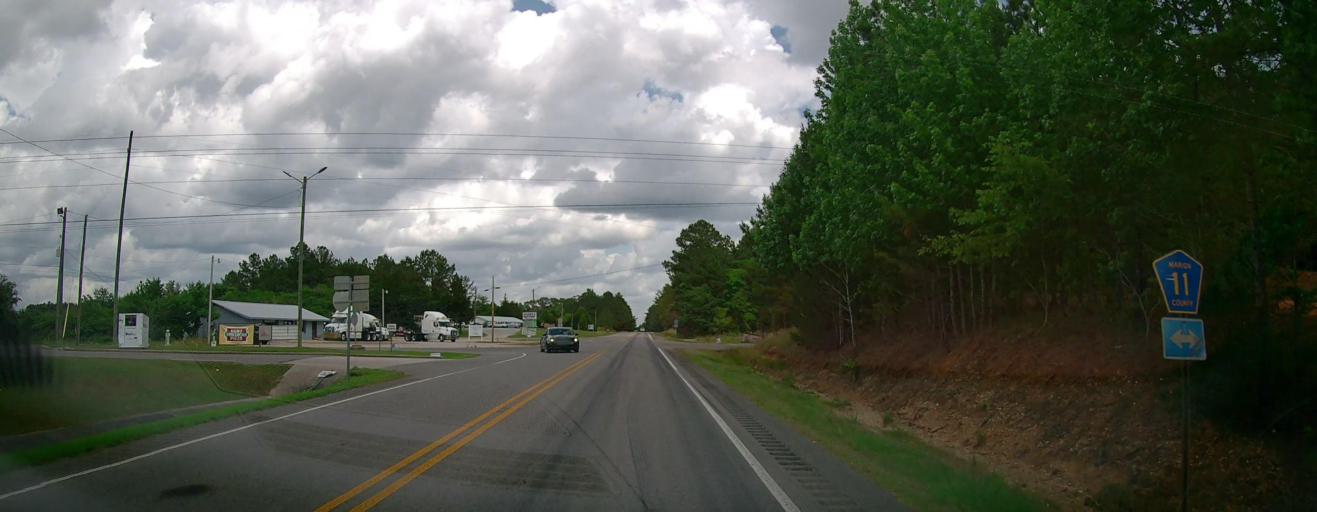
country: US
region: Alabama
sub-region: Marion County
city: Hamilton
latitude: 34.1219
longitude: -88.0419
